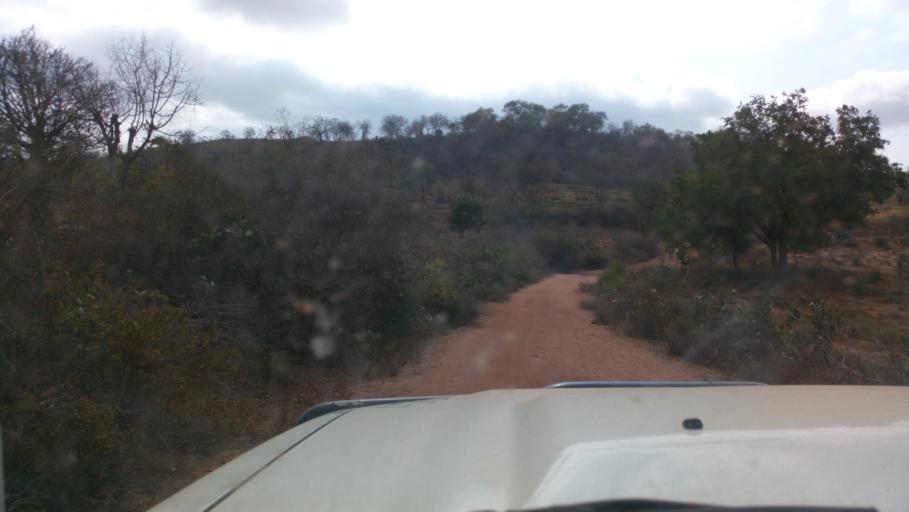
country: KE
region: Kitui
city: Kitui
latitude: -1.8568
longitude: 38.2866
